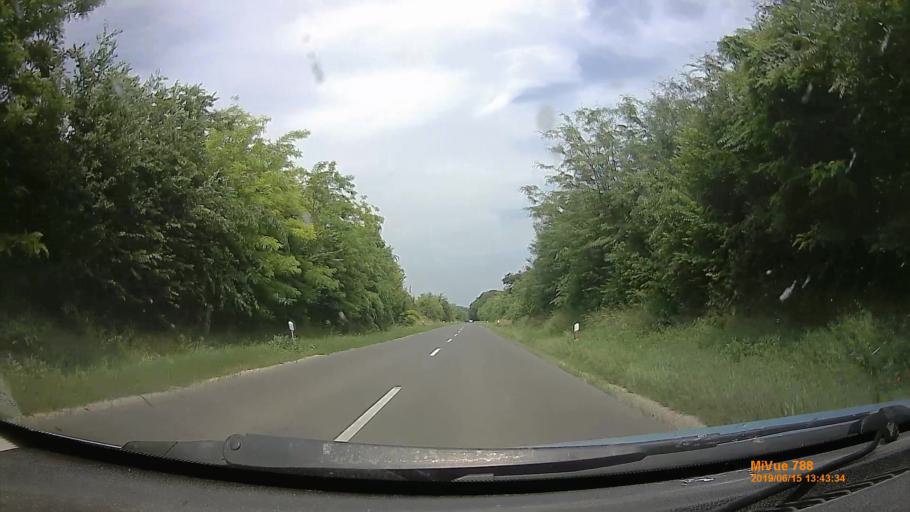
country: HU
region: Tolna
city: Iregszemcse
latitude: 46.6783
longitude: 18.1830
